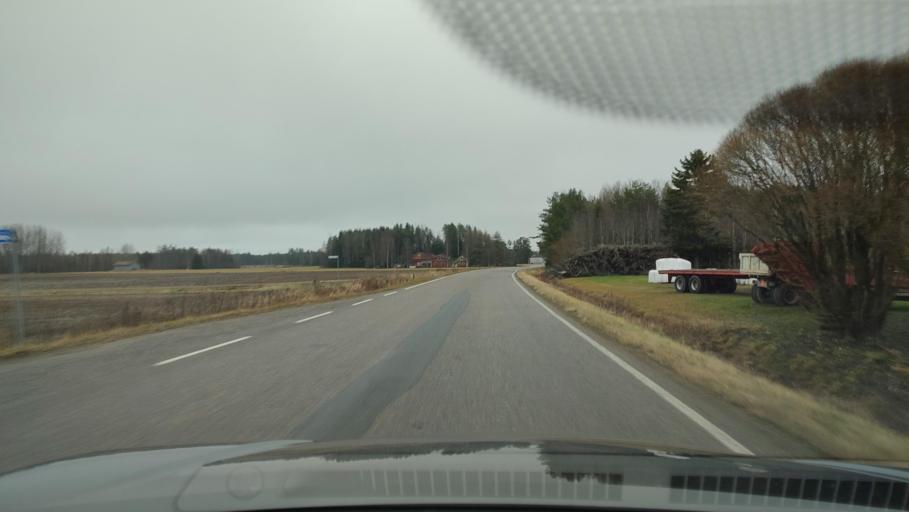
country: FI
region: Southern Ostrobothnia
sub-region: Suupohja
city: Isojoki
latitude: 62.2382
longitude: 22.0310
